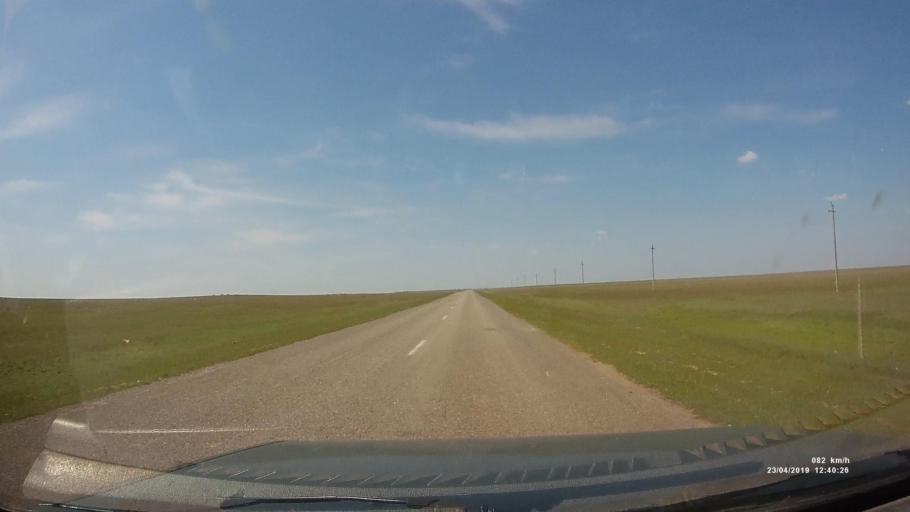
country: RU
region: Kalmykiya
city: Yashalta
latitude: 46.4402
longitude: 42.6968
